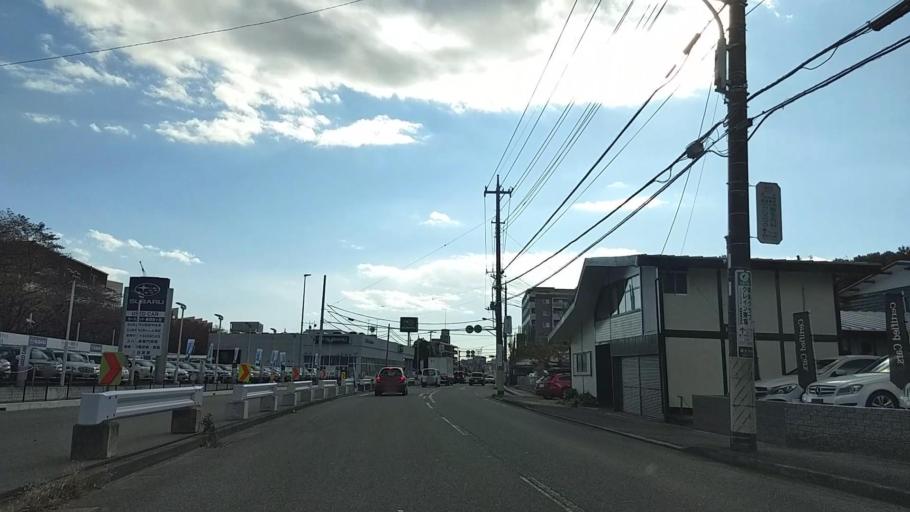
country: JP
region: Tokyo
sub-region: Machida-shi
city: Machida
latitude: 35.5965
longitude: 139.4996
